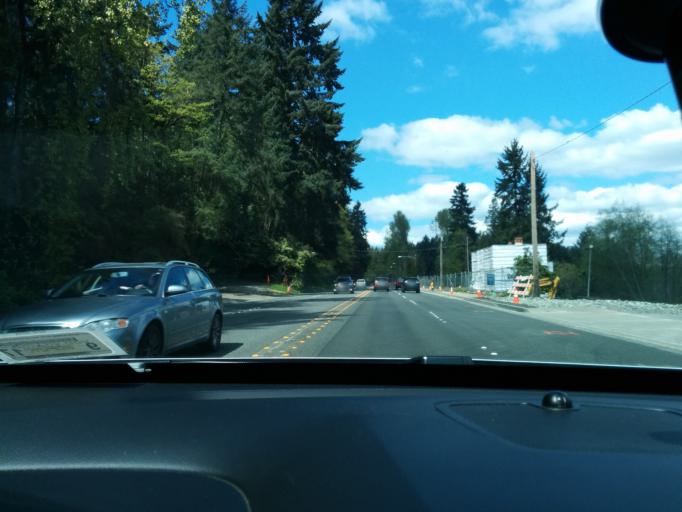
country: US
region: Washington
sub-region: King County
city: Bellevue
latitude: 47.5905
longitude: -122.1928
